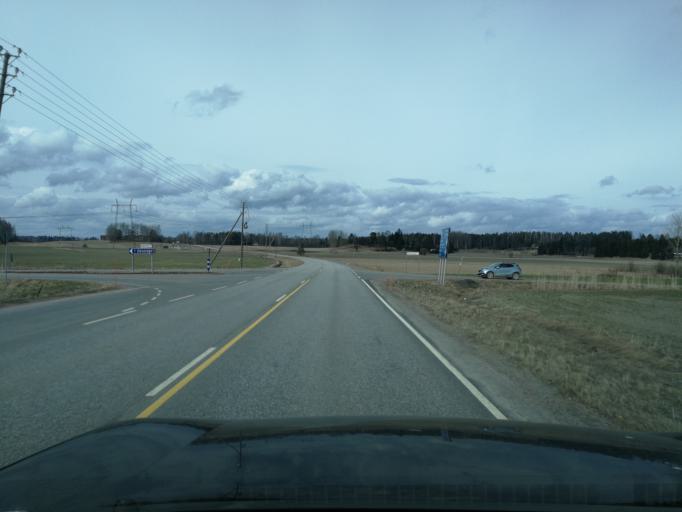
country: FI
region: Uusimaa
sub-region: Helsinki
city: Siuntio
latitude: 60.1160
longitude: 24.2412
